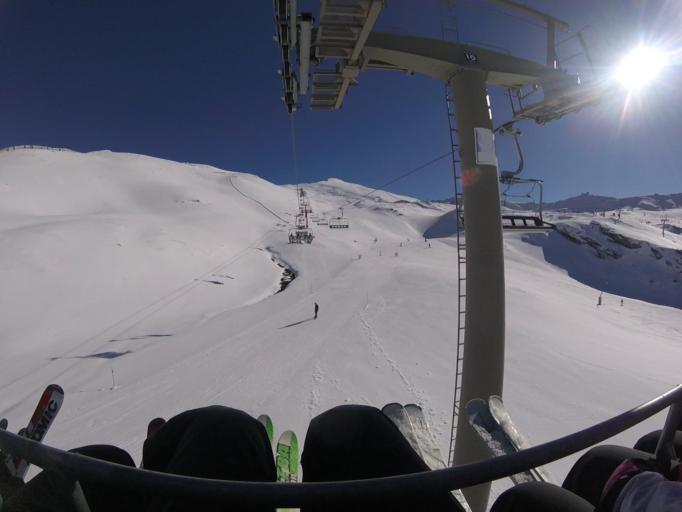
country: ES
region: Andalusia
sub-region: Provincia de Granada
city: Guejar-Sierra
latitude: 37.0732
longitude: -3.3845
